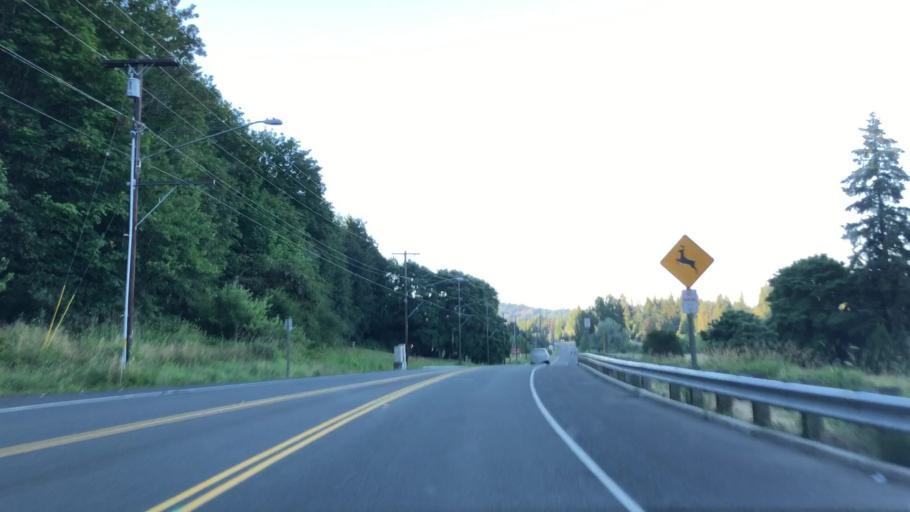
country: US
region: Washington
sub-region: King County
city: Sammamish
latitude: 47.6820
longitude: -122.0790
